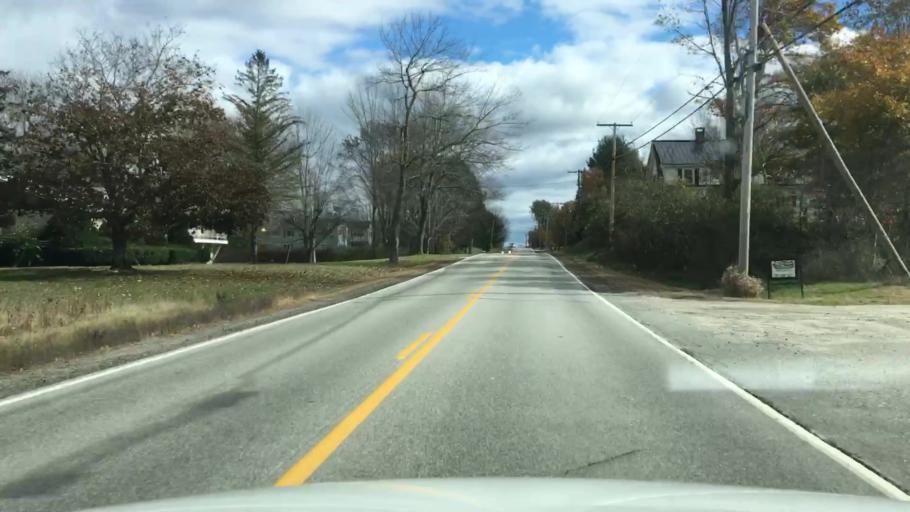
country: US
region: Maine
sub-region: Sagadahoc County
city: Richmond
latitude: 44.0936
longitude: -69.8360
